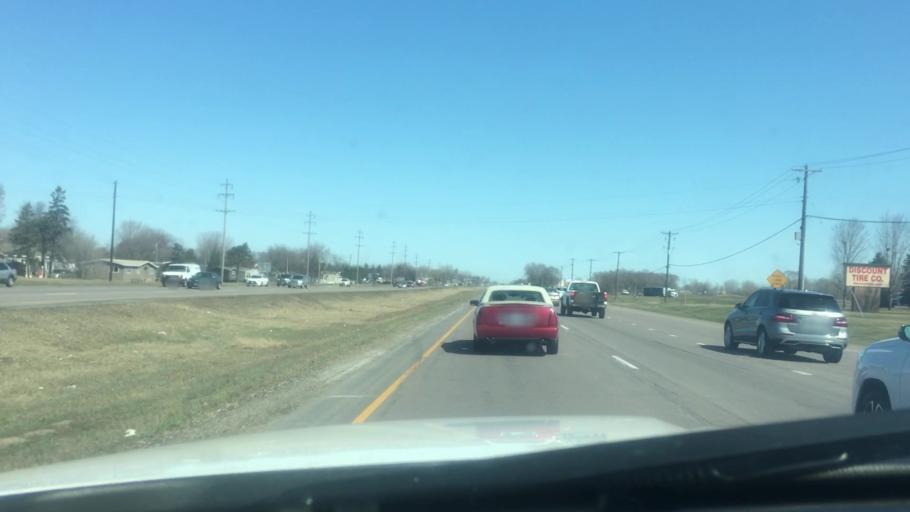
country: US
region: Minnesota
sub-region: Anoka County
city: Blaine
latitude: 45.1418
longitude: -93.2351
